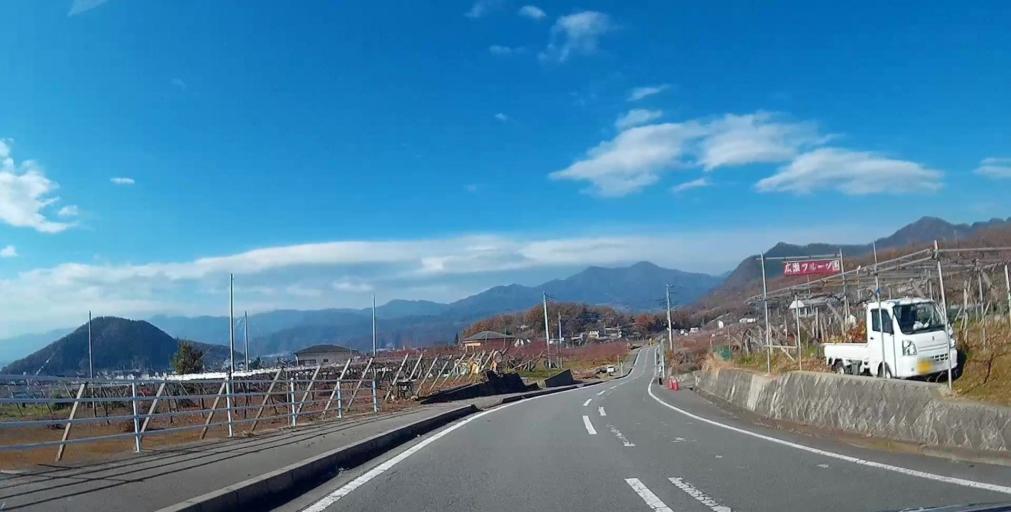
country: JP
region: Yamanashi
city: Enzan
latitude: 35.7136
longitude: 138.7432
